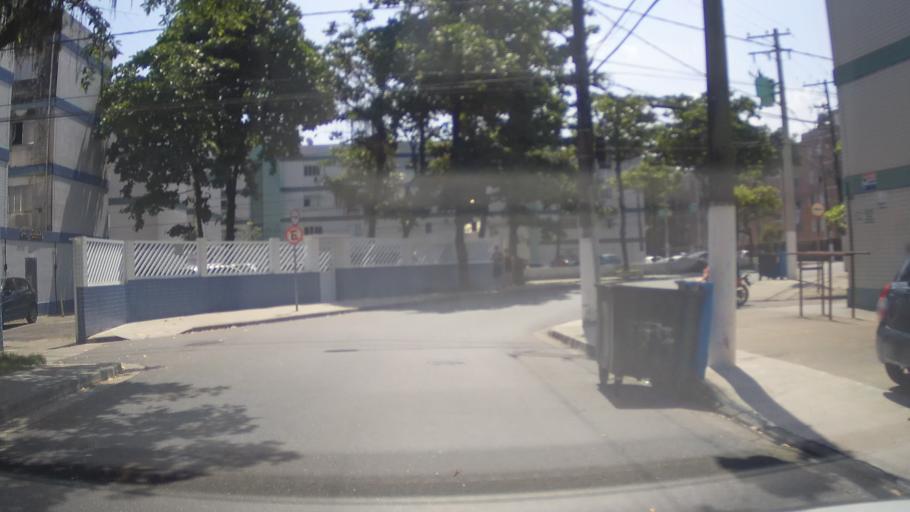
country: BR
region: Sao Paulo
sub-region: Santos
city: Santos
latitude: -23.9756
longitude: -46.3074
